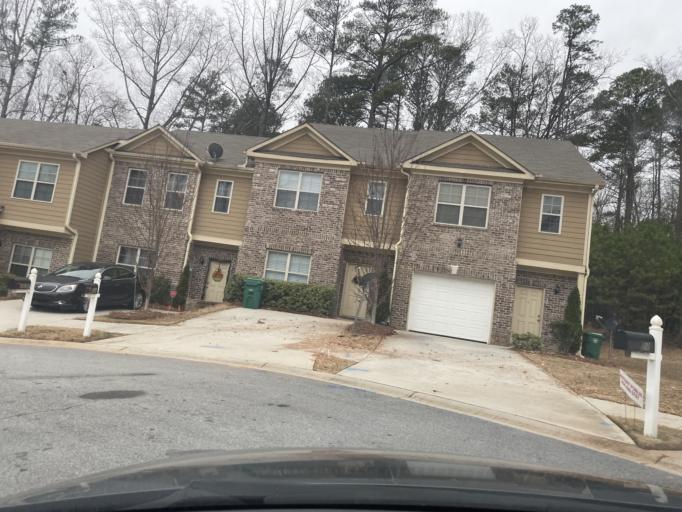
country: US
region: Georgia
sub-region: DeKalb County
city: Pine Mountain
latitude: 33.6895
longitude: -84.1557
